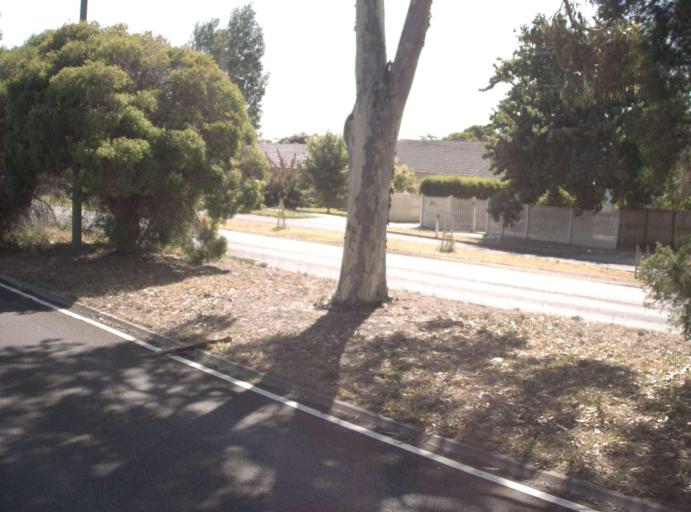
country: AU
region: Victoria
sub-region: Frankston
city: Frankston North
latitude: -38.1237
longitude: 145.1412
